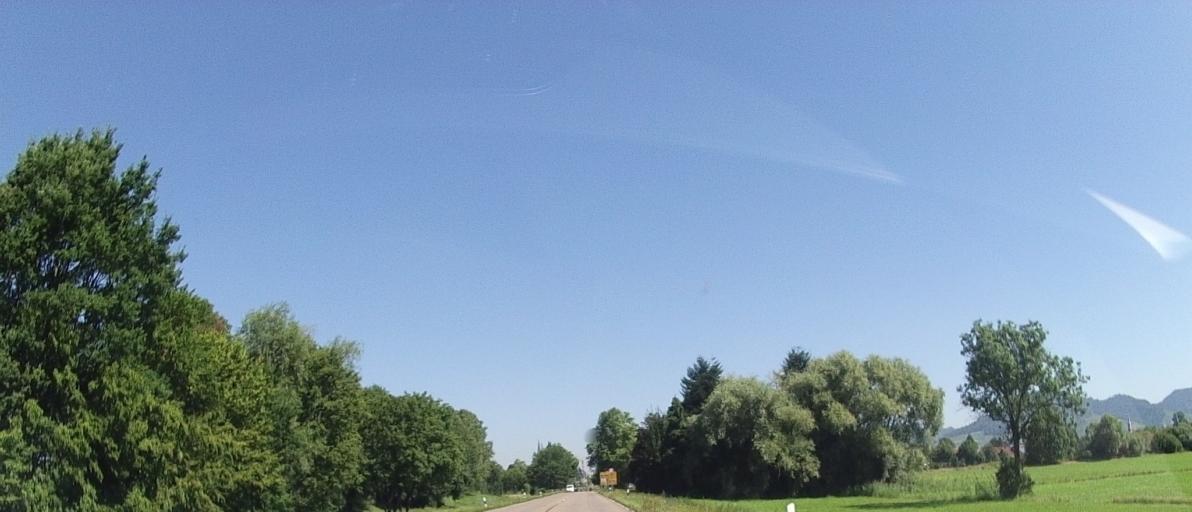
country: DE
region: Baden-Wuerttemberg
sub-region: Karlsruhe Region
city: Buhl
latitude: 48.6868
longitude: 8.1299
